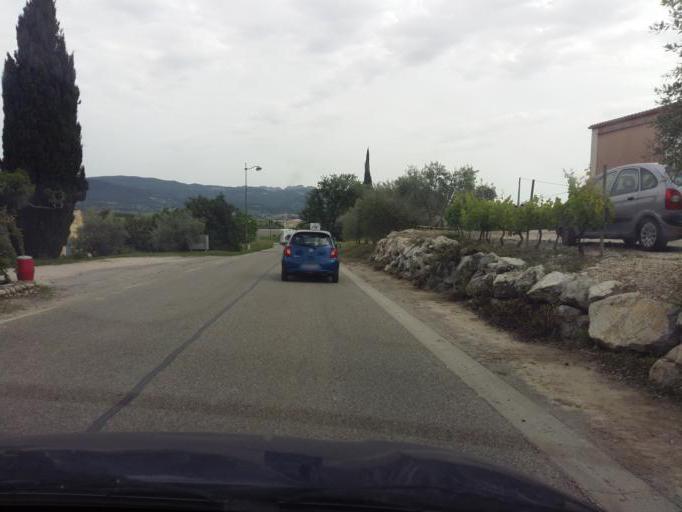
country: FR
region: Provence-Alpes-Cote d'Azur
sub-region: Departement du Vaucluse
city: Sablet
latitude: 44.2271
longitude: 4.9869
